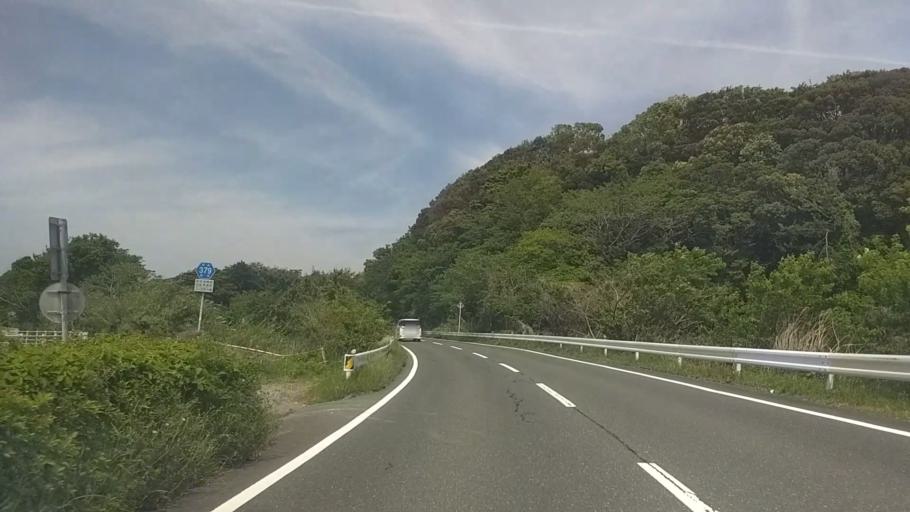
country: JP
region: Shizuoka
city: Kosai-shi
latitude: 34.7759
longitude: 137.5643
